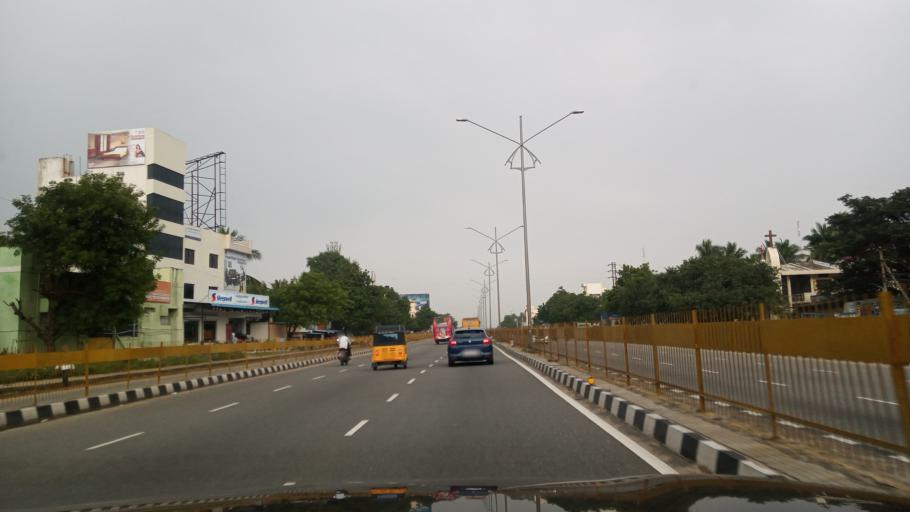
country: IN
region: Tamil Nadu
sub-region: Vellore
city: Katpadi
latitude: 12.9394
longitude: 79.1681
